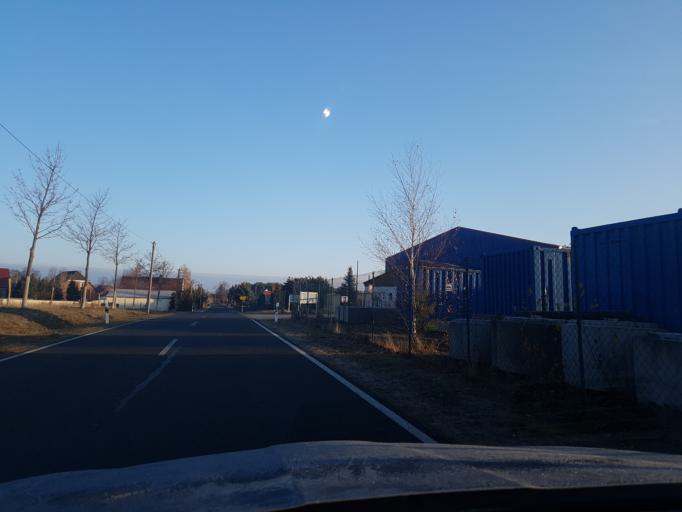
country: DE
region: Brandenburg
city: Herzberg
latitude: 51.6746
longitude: 13.3004
